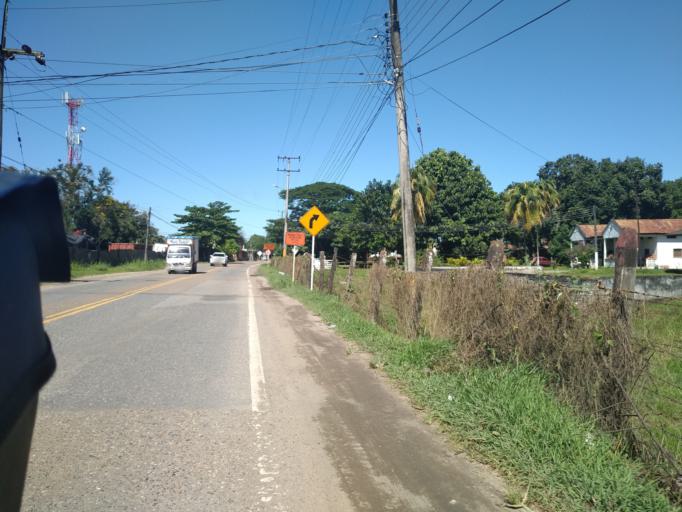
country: CO
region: Cundinamarca
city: Puerto Salgar
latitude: 5.4745
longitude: -74.6470
